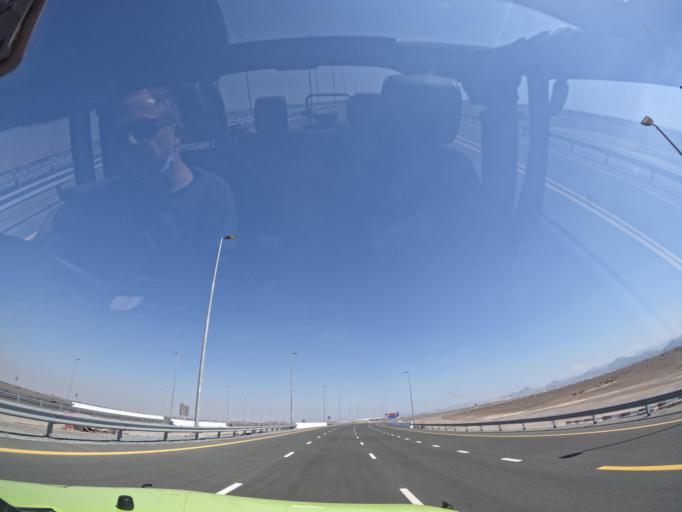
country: AE
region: Ash Shariqah
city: Adh Dhayd
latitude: 25.1126
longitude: 55.9354
